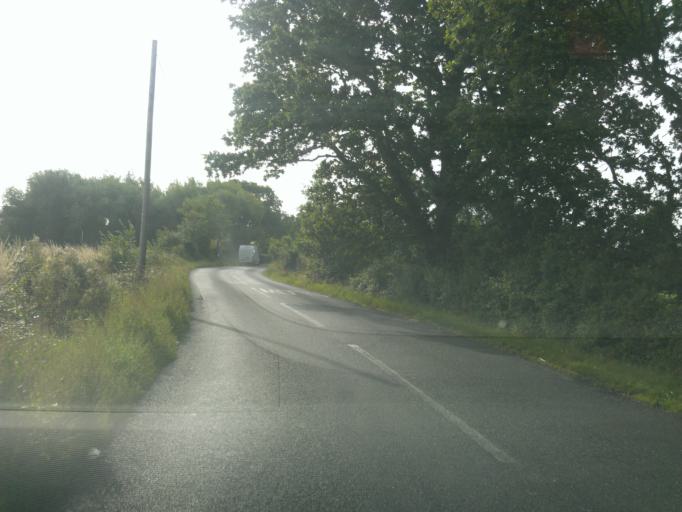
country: GB
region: England
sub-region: Essex
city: Great Bentley
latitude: 51.8343
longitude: 1.0721
